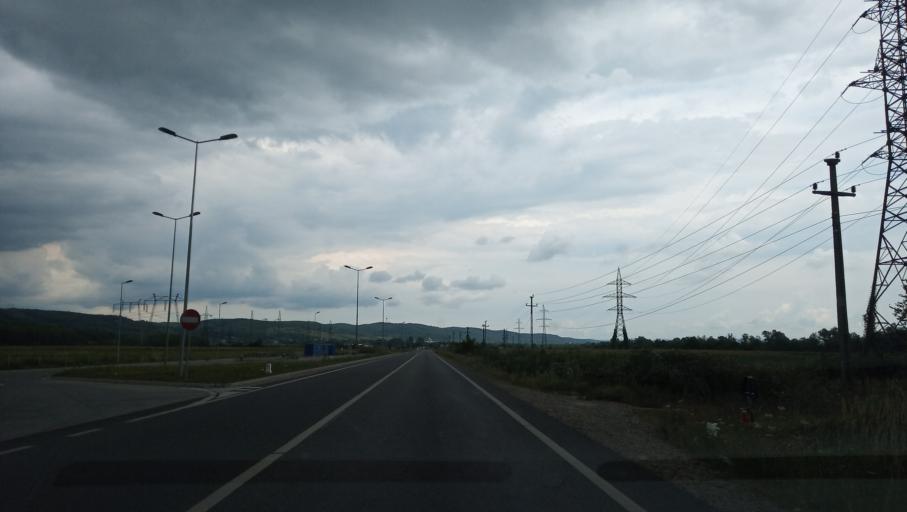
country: RO
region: Gorj
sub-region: Oras Rovinari
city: Rovinari
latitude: 44.9011
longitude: 23.1770
